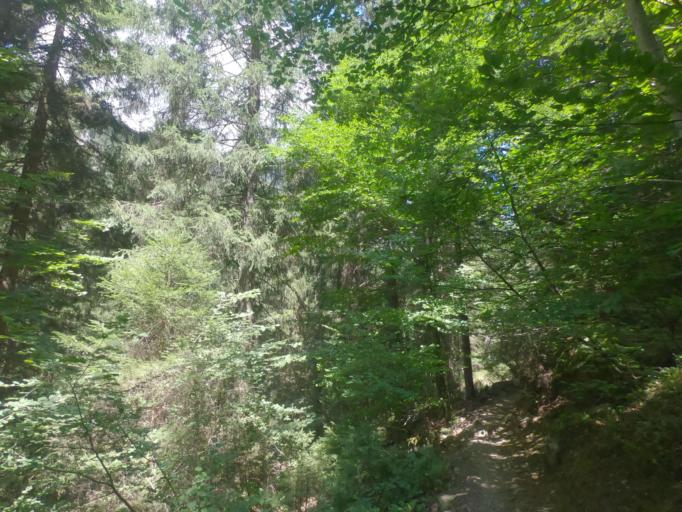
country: CH
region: Valais
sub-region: Saint-Maurice District
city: Salvan
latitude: 46.0737
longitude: 6.9724
